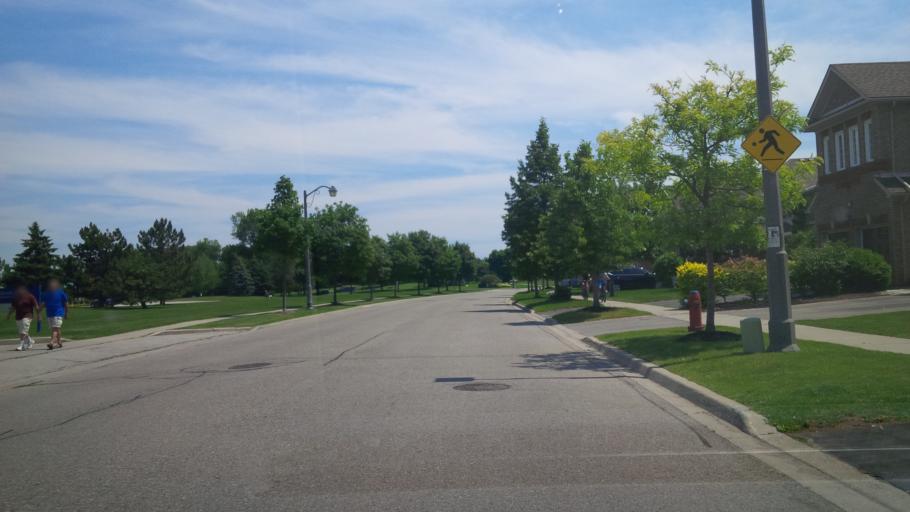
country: CA
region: Ontario
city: Burlington
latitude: 43.3958
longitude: -79.8013
